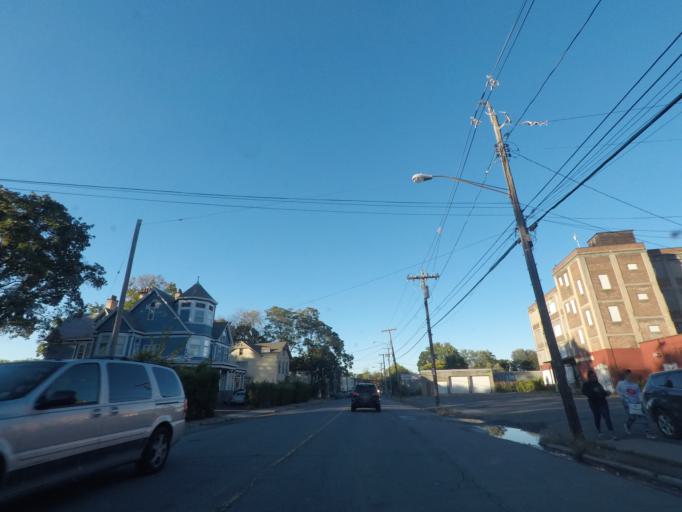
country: US
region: New York
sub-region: Albany County
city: Green Island
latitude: 42.7550
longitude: -73.6825
